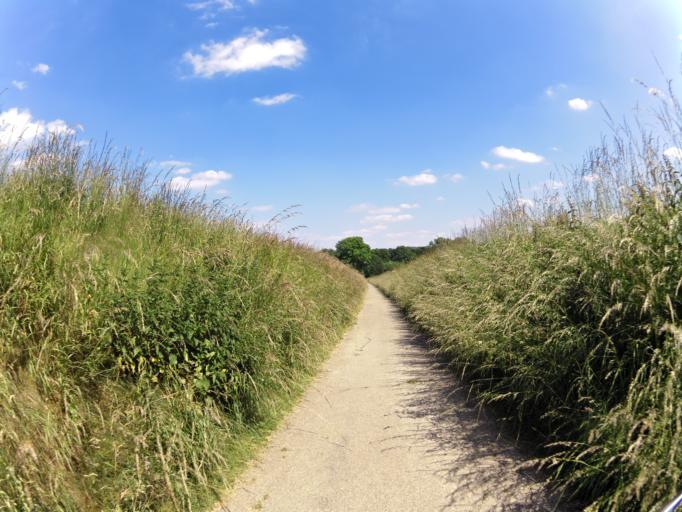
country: NL
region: Limburg
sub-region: Gemeente Kerkrade
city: Kerkrade
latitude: 50.8736
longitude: 6.0464
